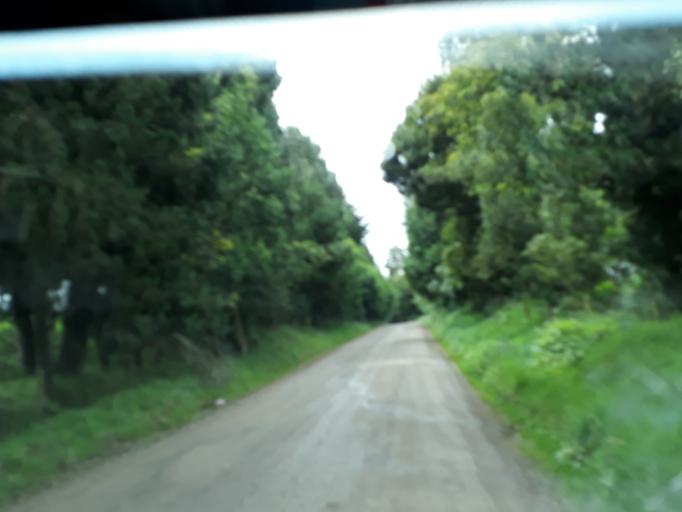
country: CO
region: Cundinamarca
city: La Mesa
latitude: 5.2033
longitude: -73.9220
